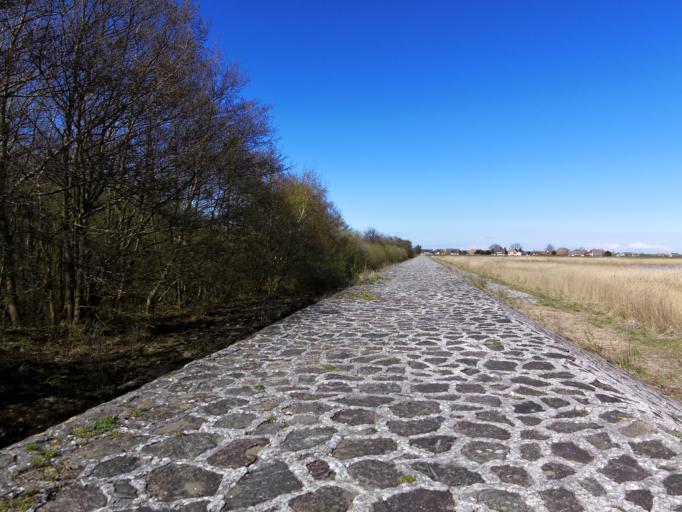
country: DE
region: Mecklenburg-Vorpommern
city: Hiddensee
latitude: 54.5169
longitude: 13.0840
